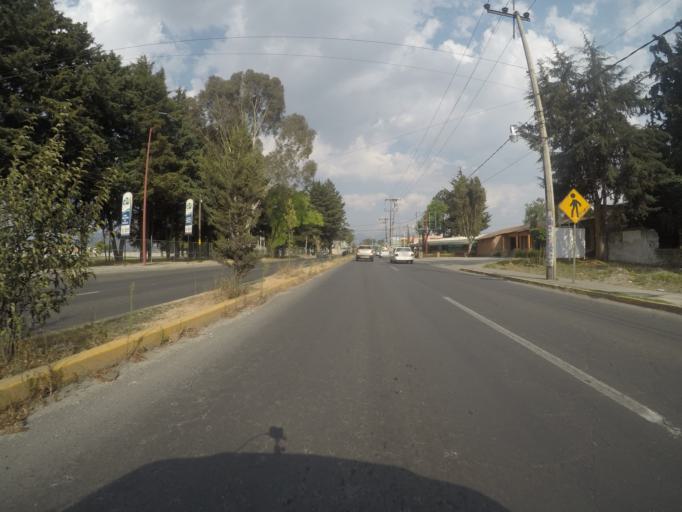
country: MX
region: Mexico
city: Santa Cruz Atizapan
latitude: 19.1834
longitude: -99.4895
